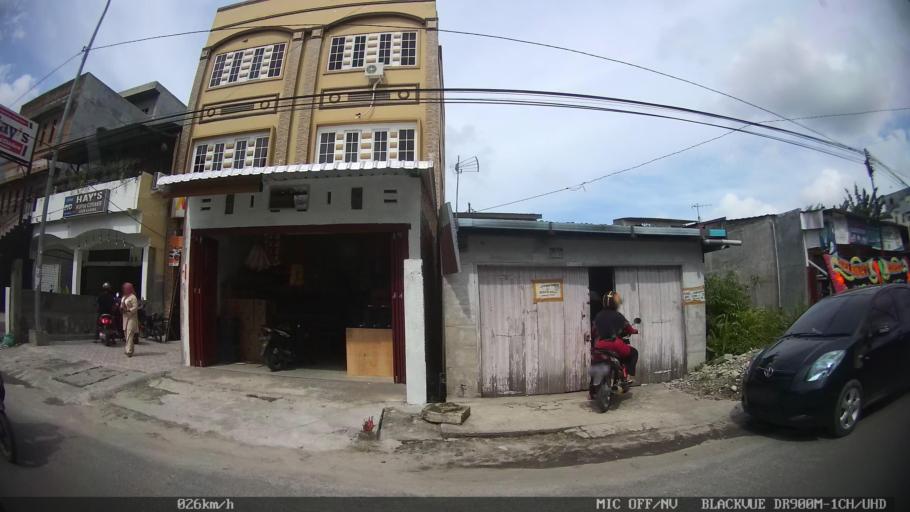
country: ID
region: North Sumatra
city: Percut
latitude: 3.5691
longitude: 98.8709
